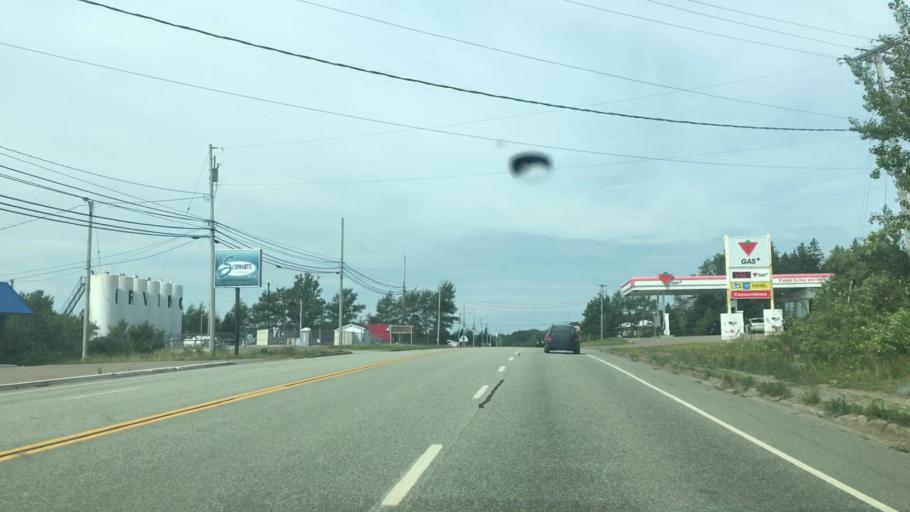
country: CA
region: Nova Scotia
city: Port Hawkesbury
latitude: 45.6401
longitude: -61.3866
